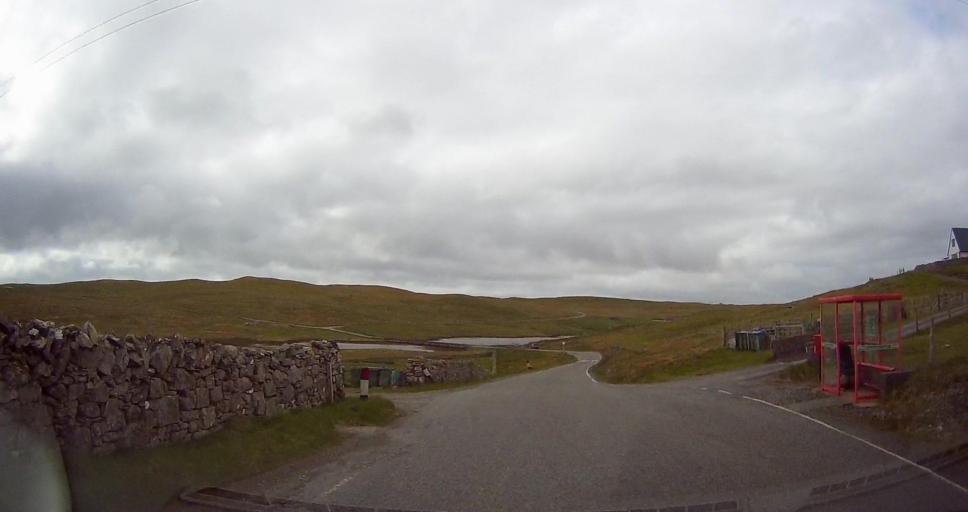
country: GB
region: Scotland
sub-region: Shetland Islands
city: Sandwick
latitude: 60.2439
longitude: -1.5235
